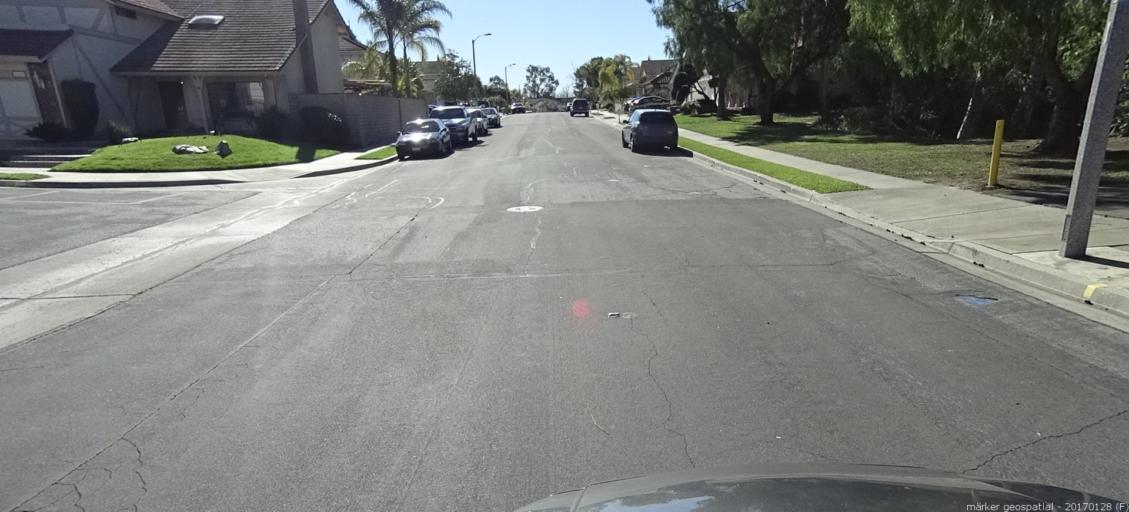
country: US
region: California
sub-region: Orange County
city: Lake Forest
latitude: 33.6541
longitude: -117.6914
